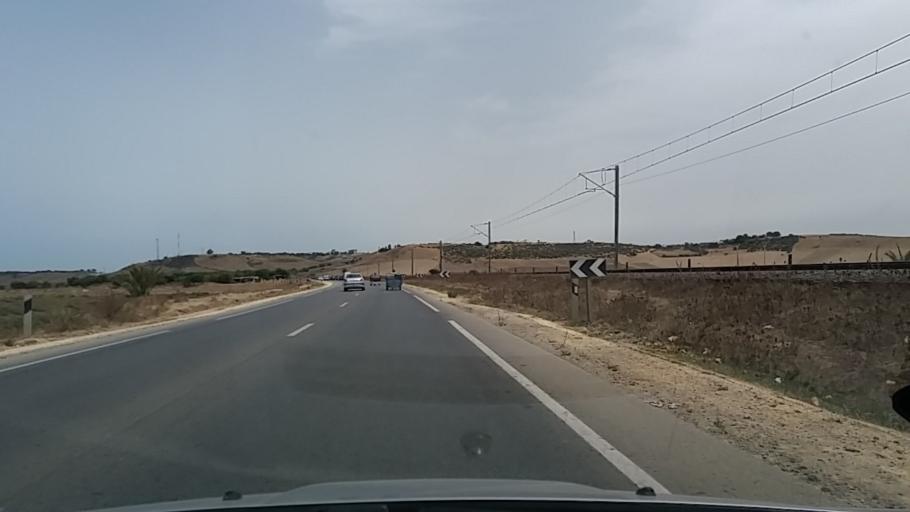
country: MA
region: Tanger-Tetouan
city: Asilah
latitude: 35.5057
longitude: -6.0024
